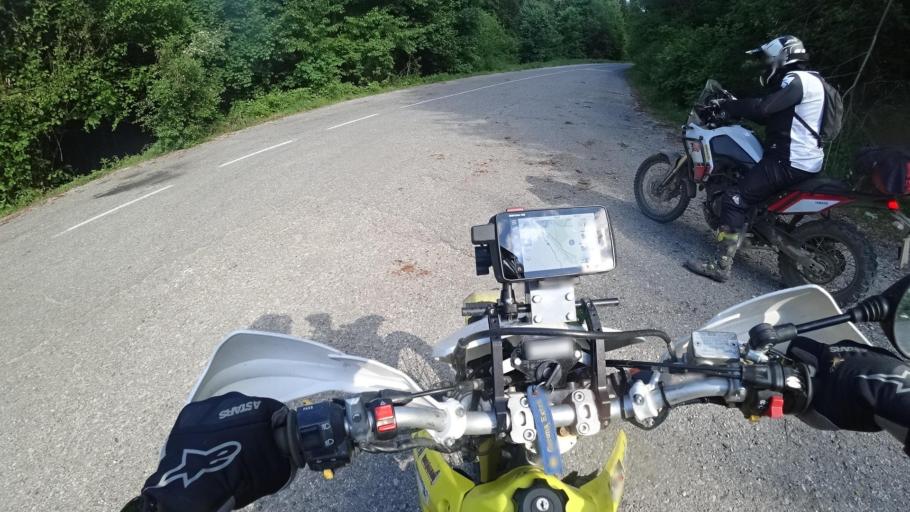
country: BA
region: Federation of Bosnia and Herzegovina
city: Sanica
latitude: 44.7255
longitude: 16.4218
